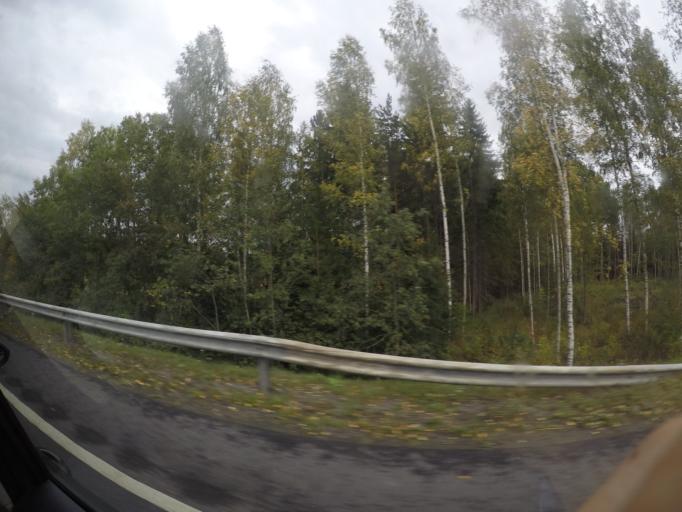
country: FI
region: Haeme
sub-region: Haemeenlinna
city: Parola
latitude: 61.1079
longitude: 24.4121
